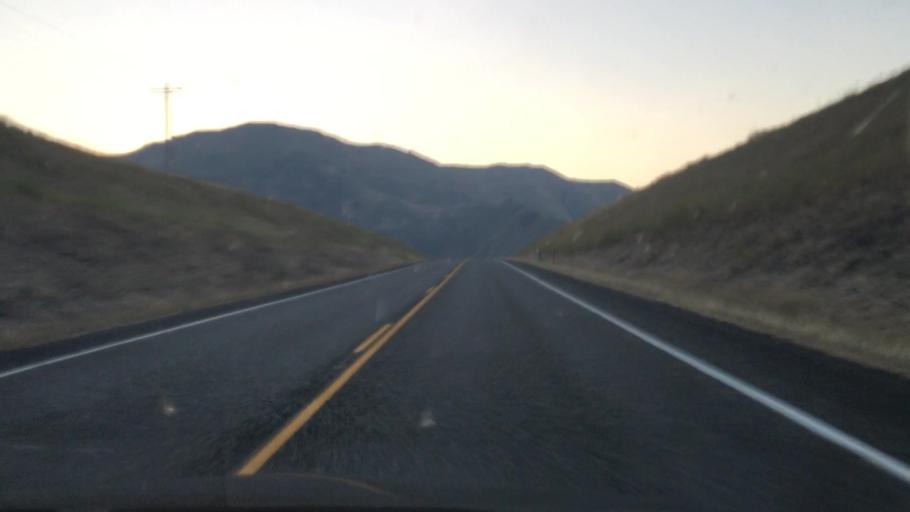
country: US
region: Idaho
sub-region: Idaho County
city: Grangeville
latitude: 45.6707
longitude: -116.3031
